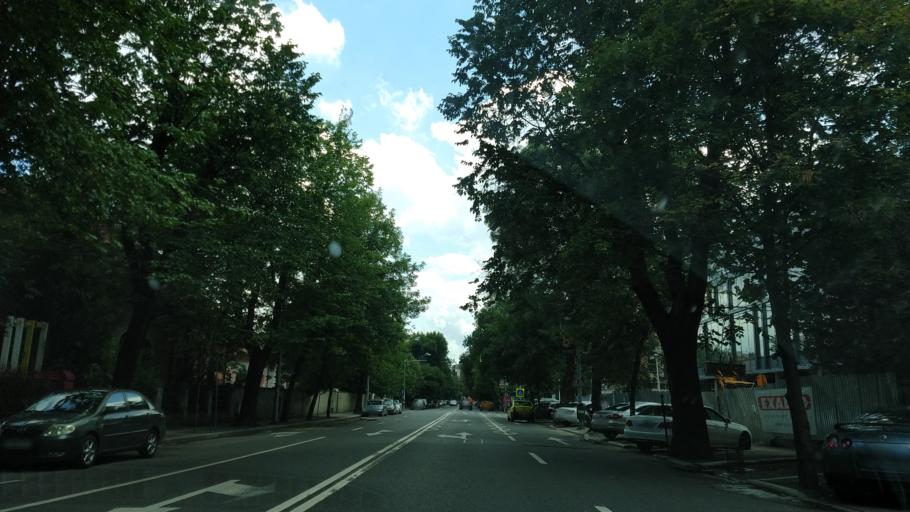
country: RO
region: Bucuresti
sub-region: Municipiul Bucuresti
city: Bucharest
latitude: 44.4609
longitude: 26.1010
